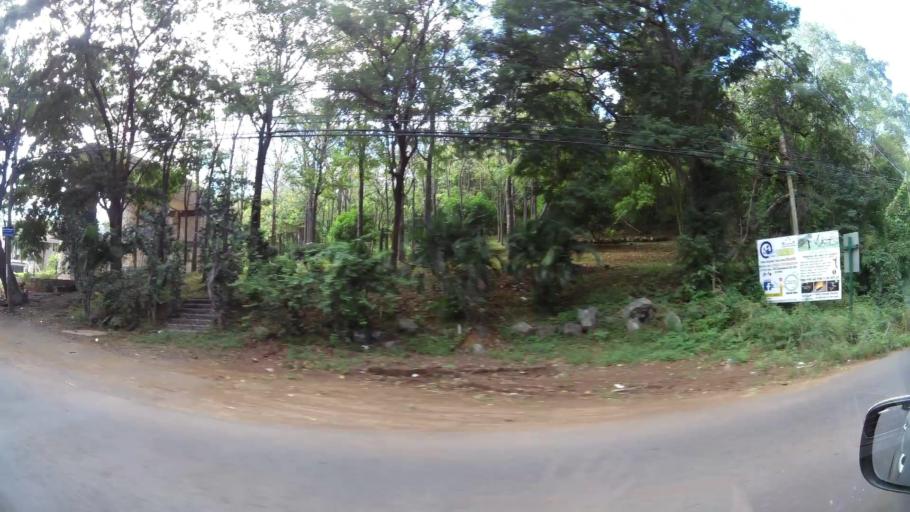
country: CR
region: Guanacaste
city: Santa Cruz
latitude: 10.3094
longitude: -85.8321
